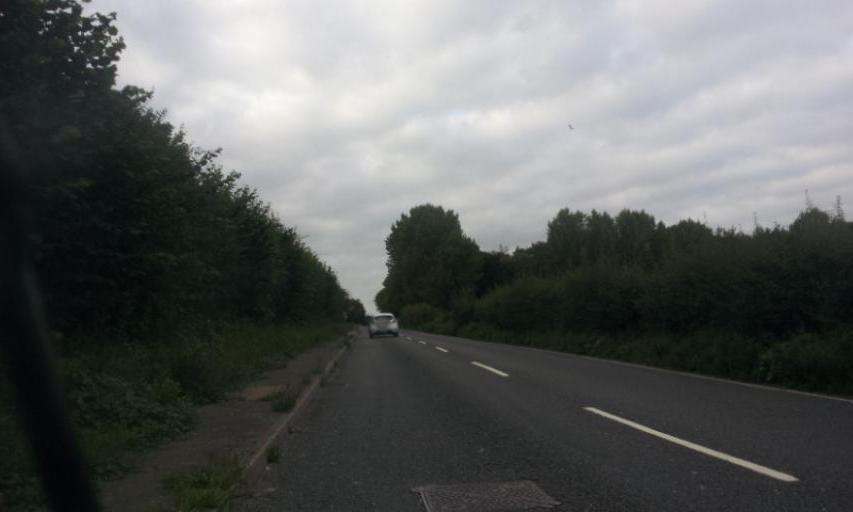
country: GB
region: England
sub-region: Kent
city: Wateringbury
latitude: 51.2398
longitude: 0.4107
